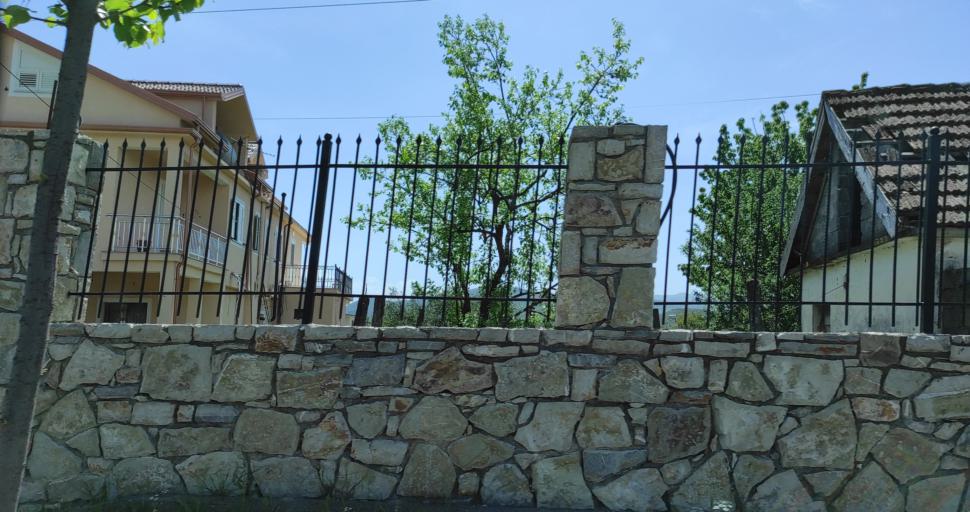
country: AL
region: Shkoder
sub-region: Rrethi i Shkodres
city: Shkoder
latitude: 42.1042
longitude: 19.5559
